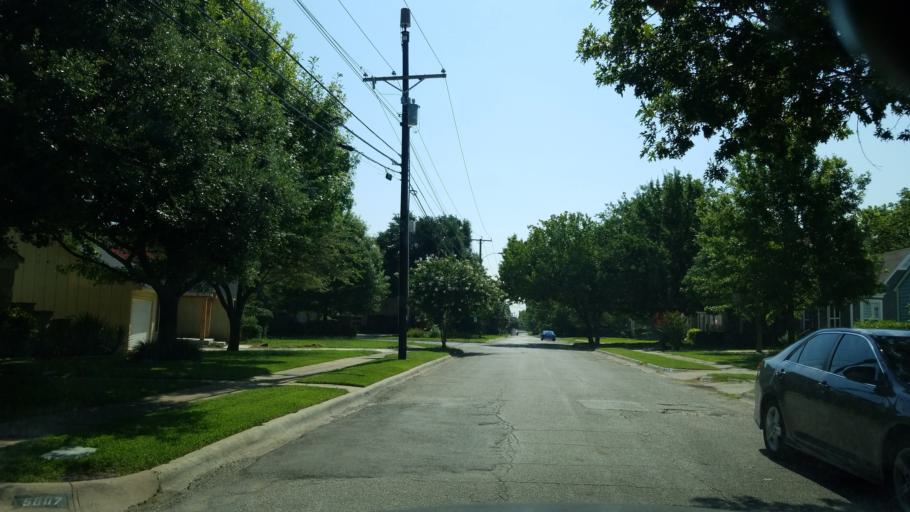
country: US
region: Texas
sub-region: Dallas County
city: Highland Park
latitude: 32.8383
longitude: -96.7675
